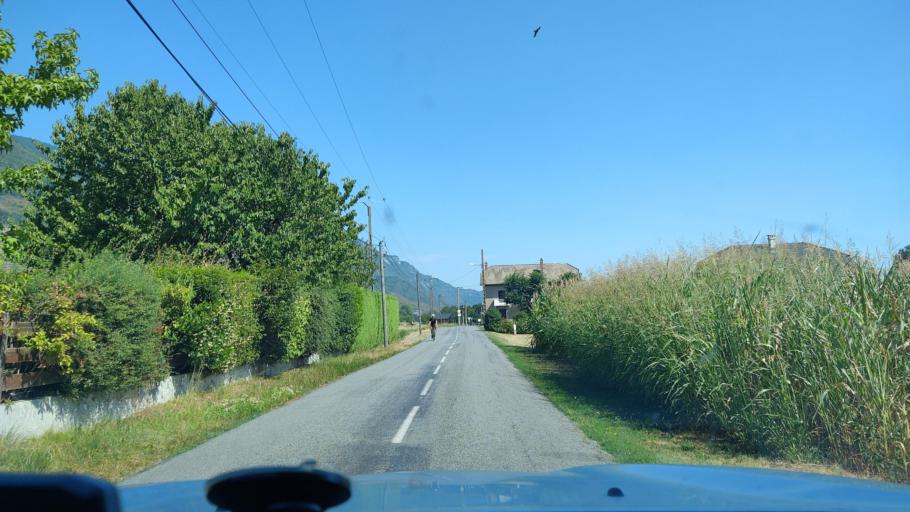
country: FR
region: Rhone-Alpes
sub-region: Departement de la Savoie
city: Le Bourget-du-Lac
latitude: 45.6168
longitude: 5.8493
